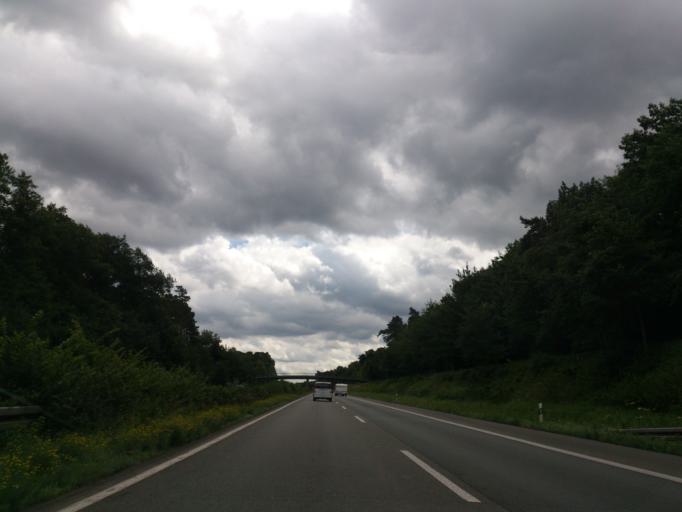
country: DE
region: North Rhine-Westphalia
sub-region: Regierungsbezirk Detmold
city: Verl
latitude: 51.9329
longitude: 8.5734
